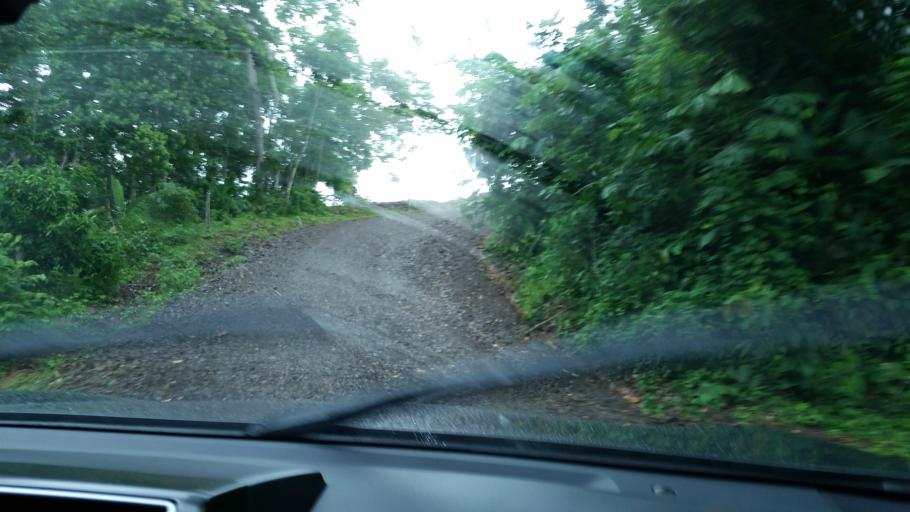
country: NI
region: Atlantico Norte (RAAN)
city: Waslala
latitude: 13.1655
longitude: -85.4147
